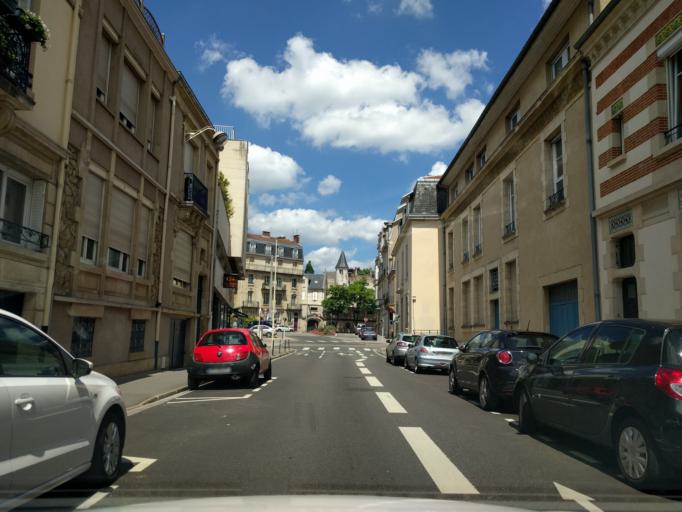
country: FR
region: Lorraine
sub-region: Departement de Meurthe-et-Moselle
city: Nancy
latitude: 48.6854
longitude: 6.1678
